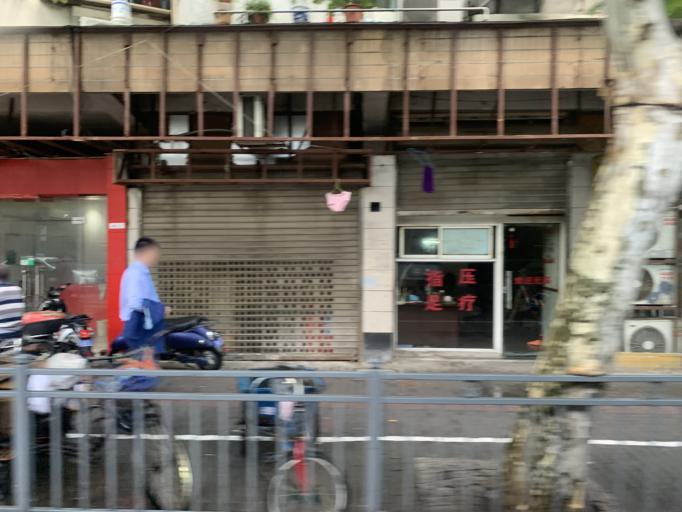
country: CN
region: Shanghai Shi
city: Luwan
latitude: 31.2139
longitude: 121.4731
